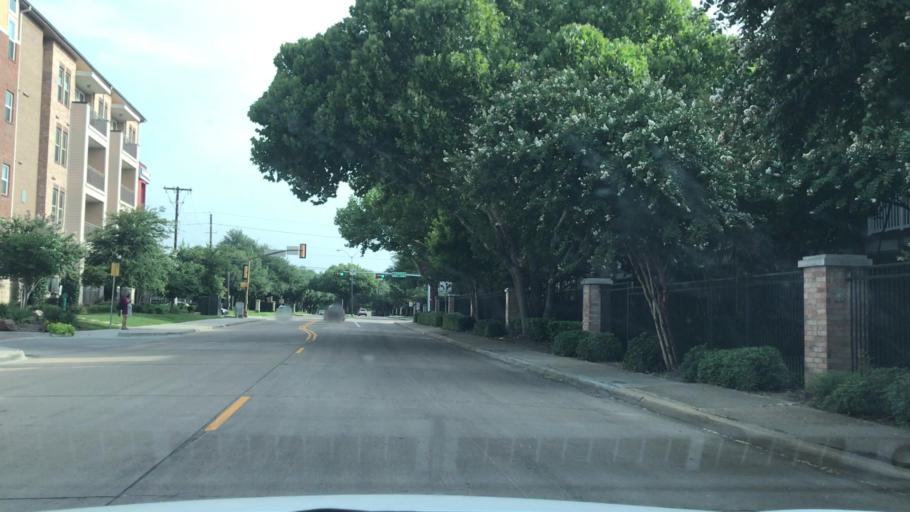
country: US
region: Texas
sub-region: Dallas County
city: Highland Park
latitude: 32.8500
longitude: -96.7645
